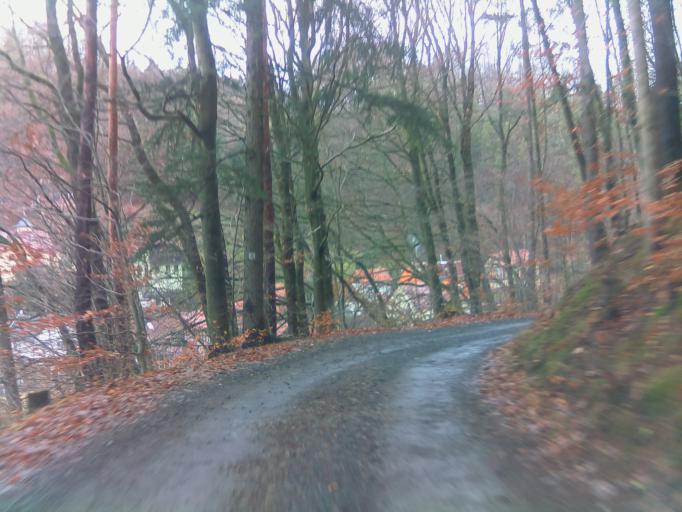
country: DE
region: Thuringia
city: Hummelshain
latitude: 50.7456
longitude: 11.6408
